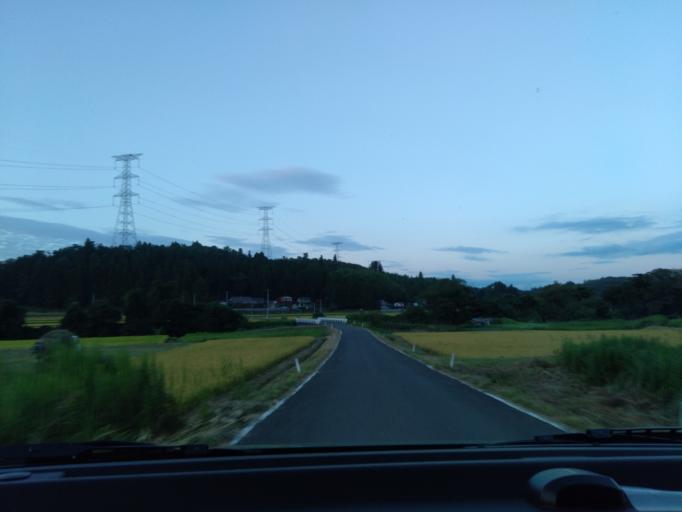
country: JP
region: Iwate
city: Ichinoseki
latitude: 38.8591
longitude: 141.1440
